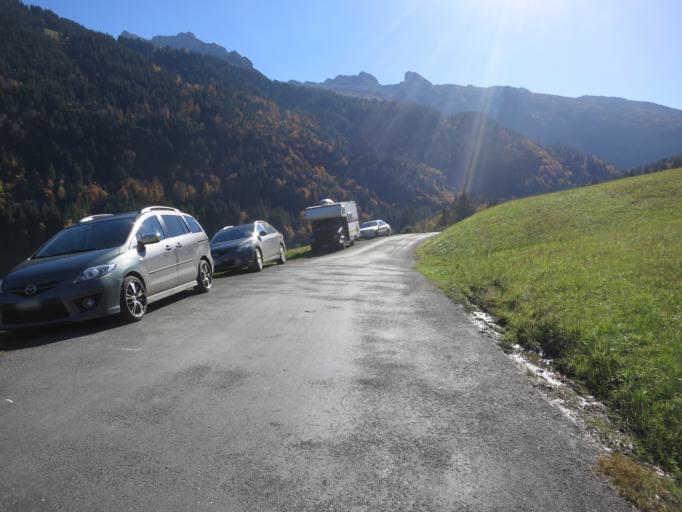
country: CH
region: Schwyz
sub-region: Bezirk March
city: Vorderthal
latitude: 47.0734
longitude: 8.9128
